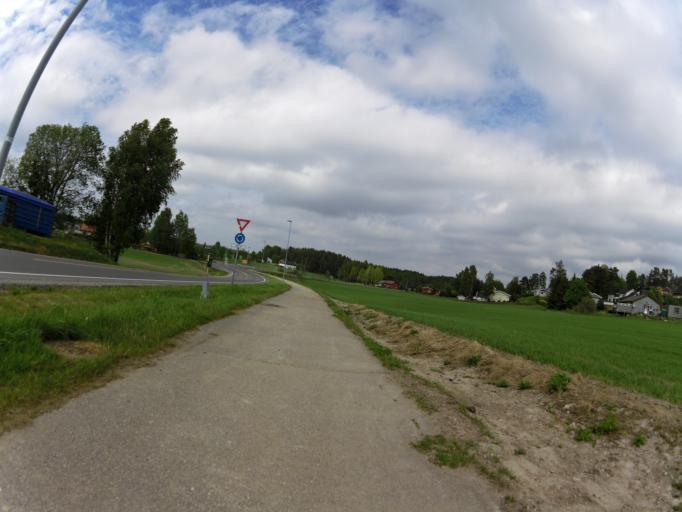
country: NO
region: Ostfold
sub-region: Rade
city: Karlshus
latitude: 59.3437
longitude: 10.9324
